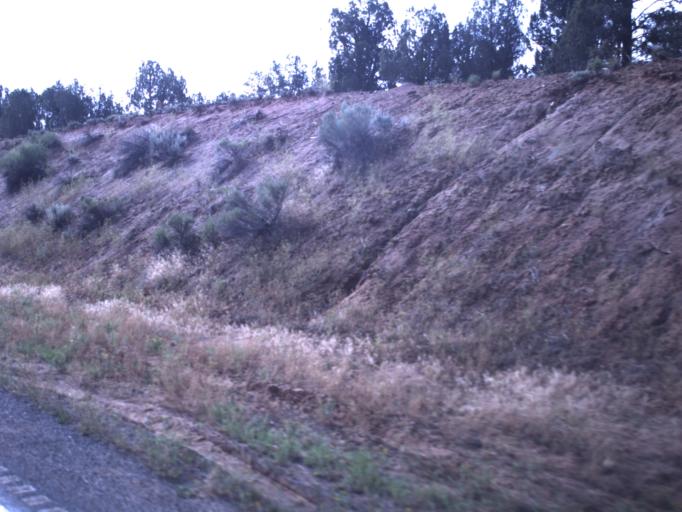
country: US
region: Utah
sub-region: Kane County
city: Kanab
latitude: 37.2195
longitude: -112.6978
